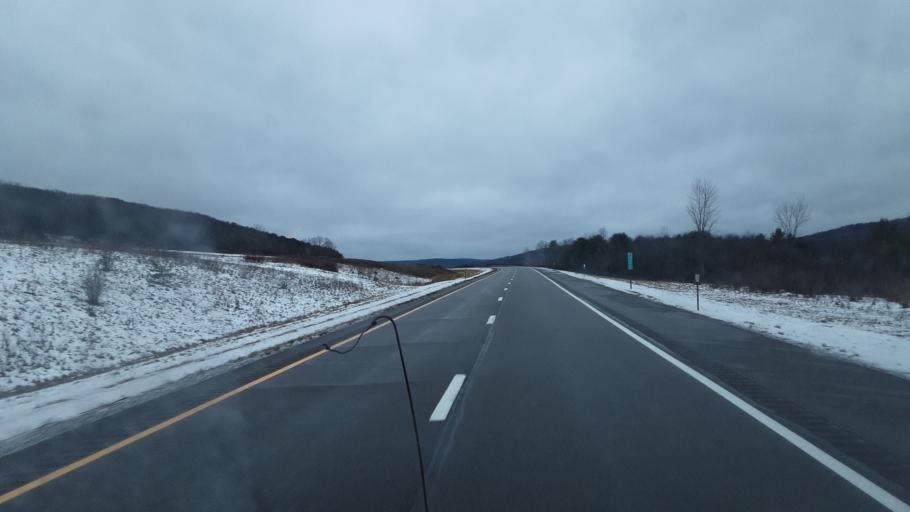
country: US
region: New York
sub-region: Allegany County
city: Alfred
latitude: 42.3165
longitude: -77.7674
